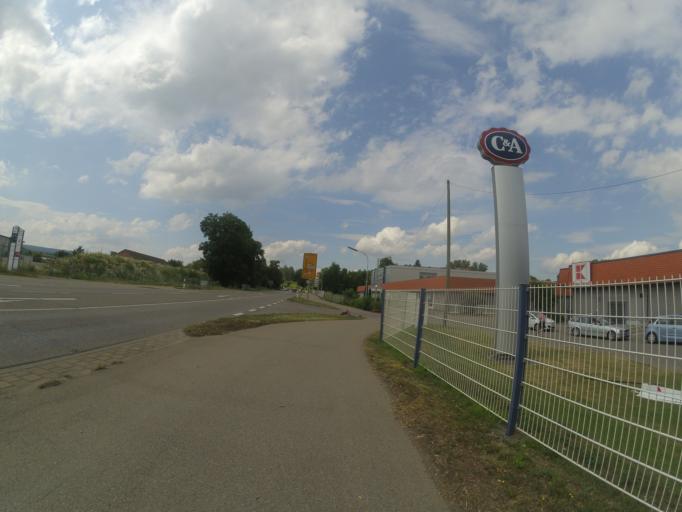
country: DE
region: Baden-Wuerttemberg
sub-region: Tuebingen Region
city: Dettingen
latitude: 48.2713
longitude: 9.7260
